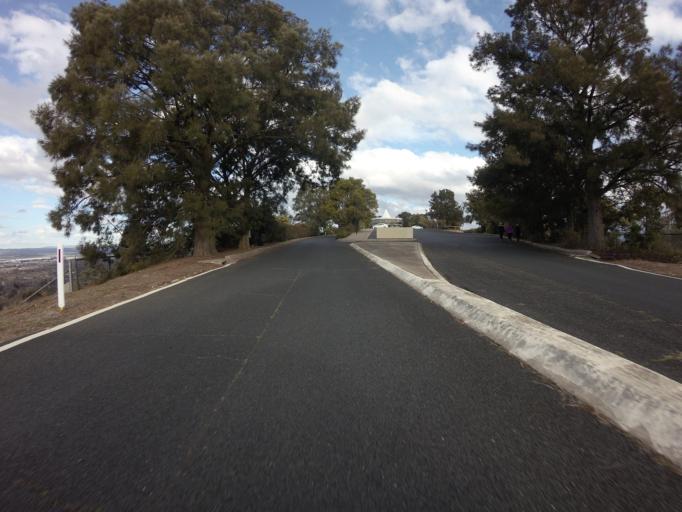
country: AU
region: Australian Capital Territory
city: Forrest
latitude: -35.3274
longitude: 149.1162
